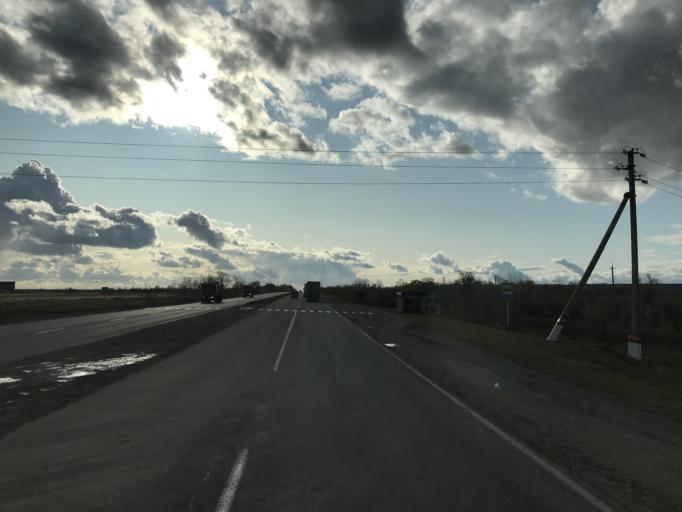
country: KZ
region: Qostanay
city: Rudnyy
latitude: 53.0122
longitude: 63.3066
